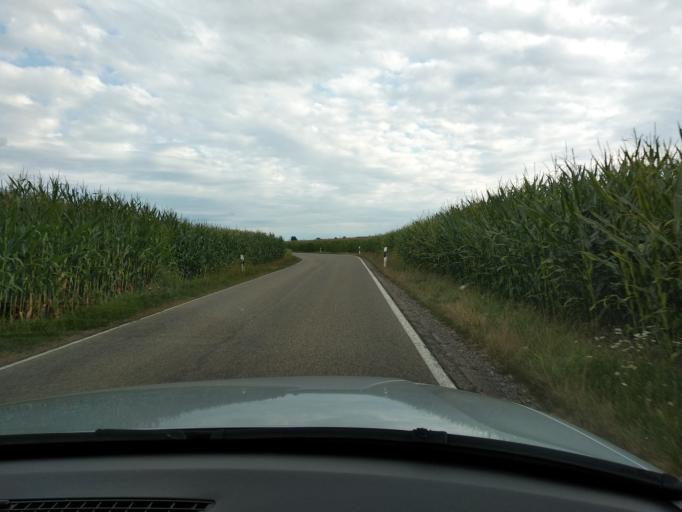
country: DE
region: Bavaria
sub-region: Swabia
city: Benningen
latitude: 47.9778
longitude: 10.2102
